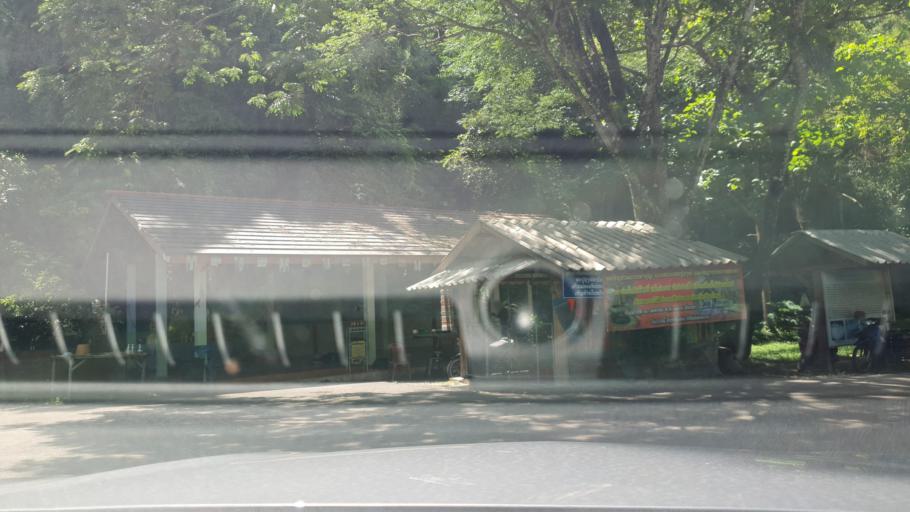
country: TH
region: Chiang Mai
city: Mae On
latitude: 18.7145
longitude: 99.2345
